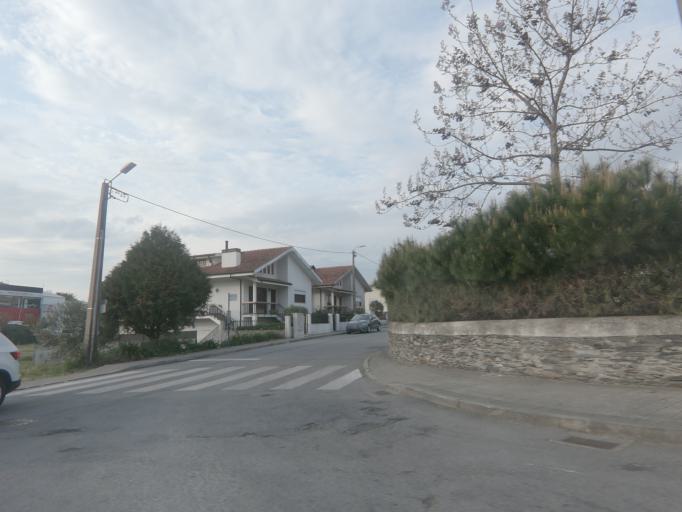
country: PT
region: Porto
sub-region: Valongo
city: Valongo
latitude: 41.1876
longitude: -8.4896
